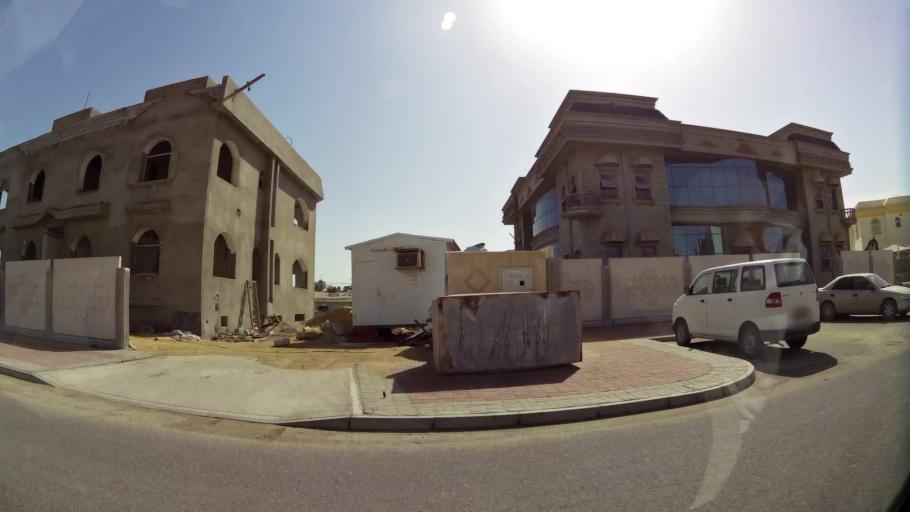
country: QA
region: Baladiyat ad Dawhah
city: Doha
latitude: 25.3565
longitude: 51.5192
